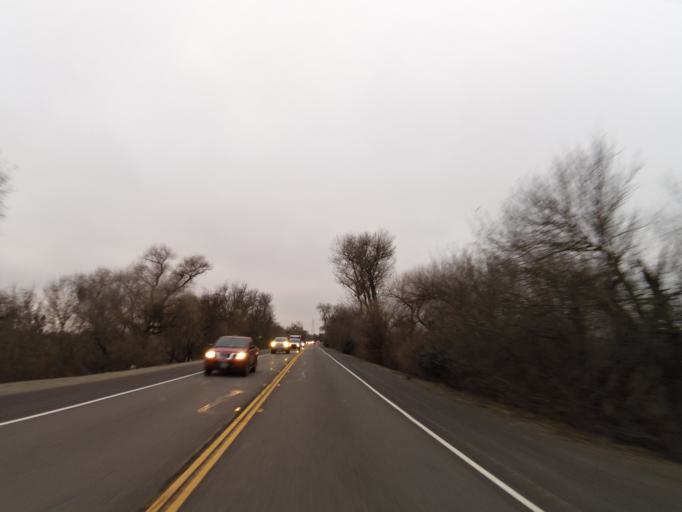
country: US
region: California
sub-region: San Joaquin County
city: Ripon
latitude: 37.6384
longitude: -121.1963
